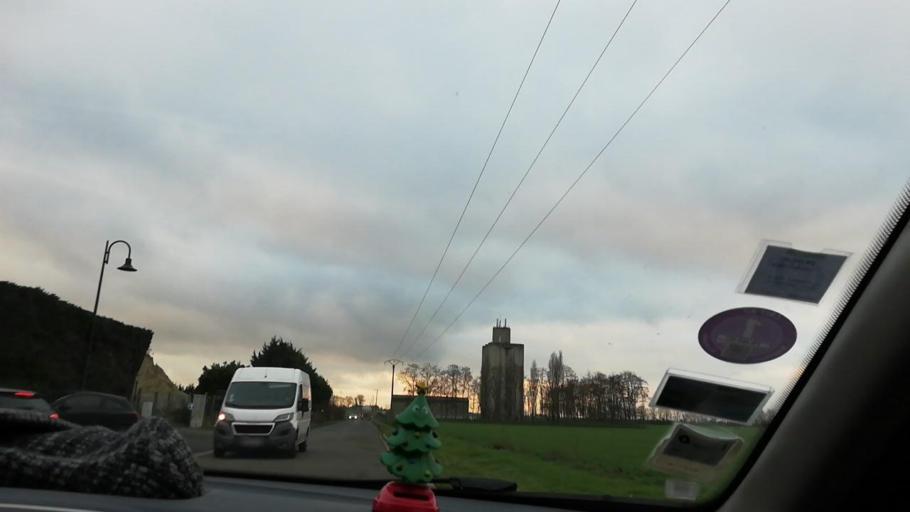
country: FR
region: Ile-de-France
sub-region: Departement de Seine-et-Marne
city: Charny
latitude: 48.9688
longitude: 2.7536
